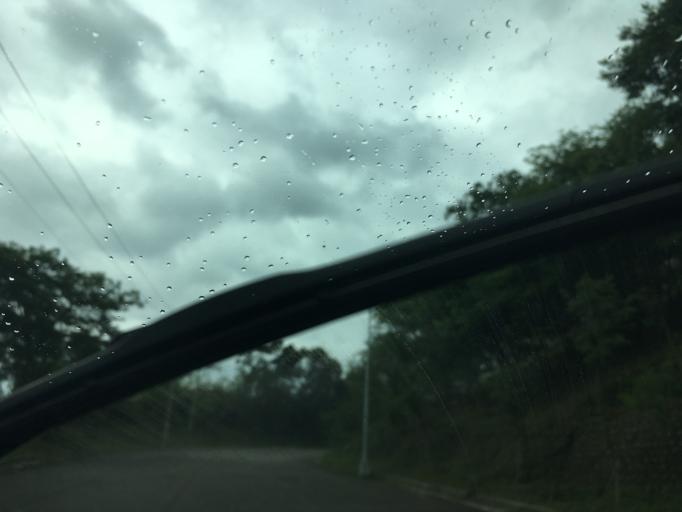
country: TW
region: Taiwan
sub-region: Taichung City
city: Taichung
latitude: 24.0653
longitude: 120.7182
